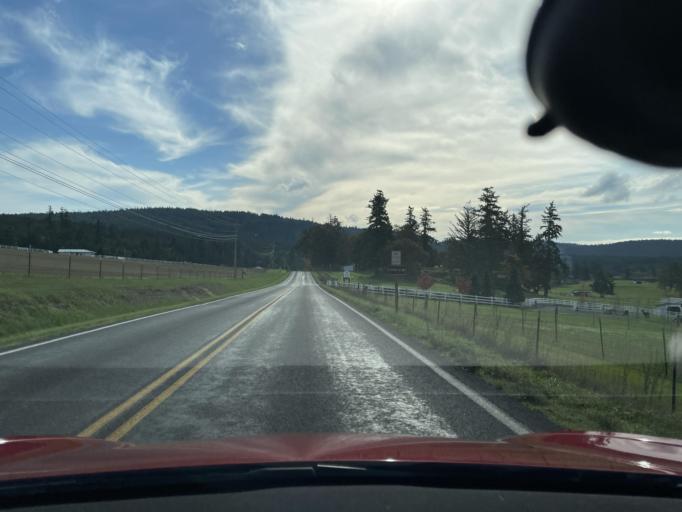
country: US
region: Washington
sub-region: San Juan County
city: Friday Harbor
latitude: 48.5776
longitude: -123.1418
